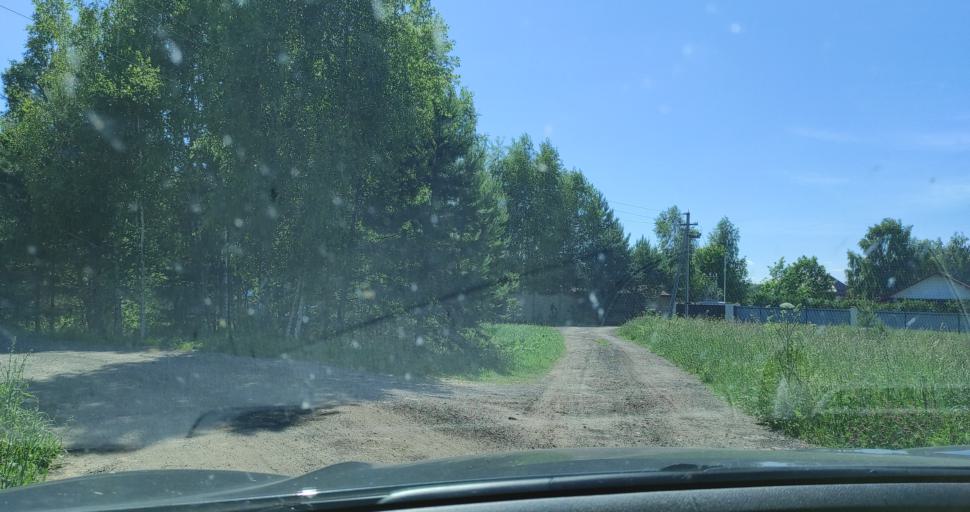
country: RU
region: Rjazan
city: Murmino
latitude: 54.5617
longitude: 40.0981
